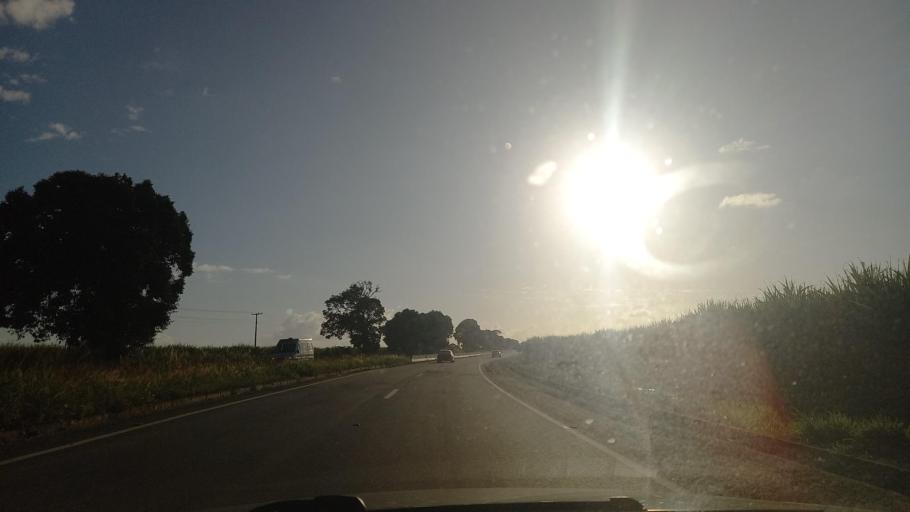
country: BR
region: Alagoas
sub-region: Campo Alegre
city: Campo Alegre
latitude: -9.7985
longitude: -36.2939
